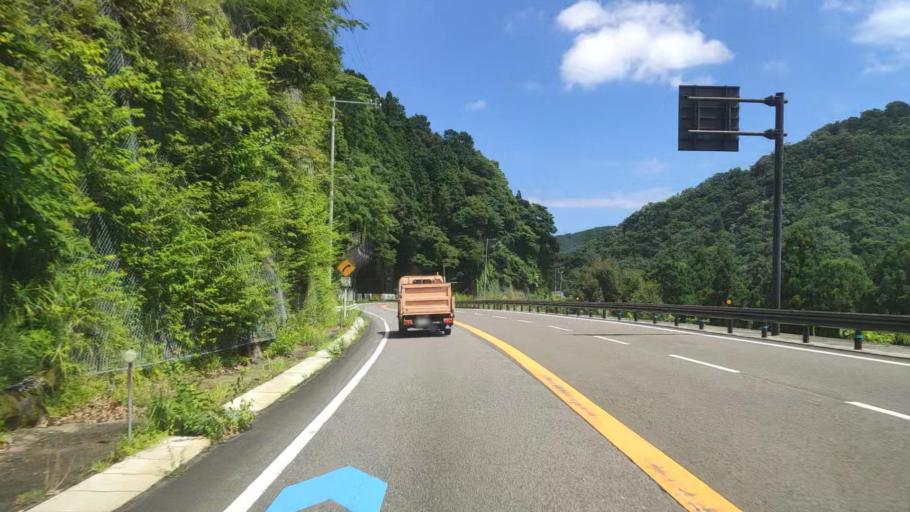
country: JP
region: Mie
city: Owase
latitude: 33.9230
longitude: 136.0953
